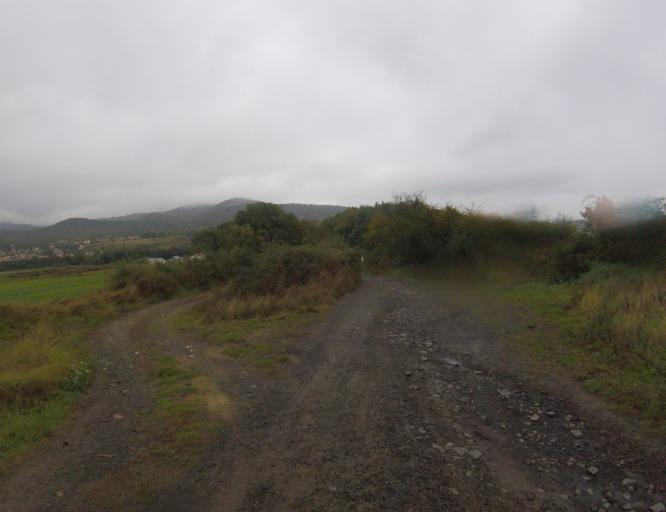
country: HU
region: Pest
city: Szob
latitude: 47.8569
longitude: 18.8788
